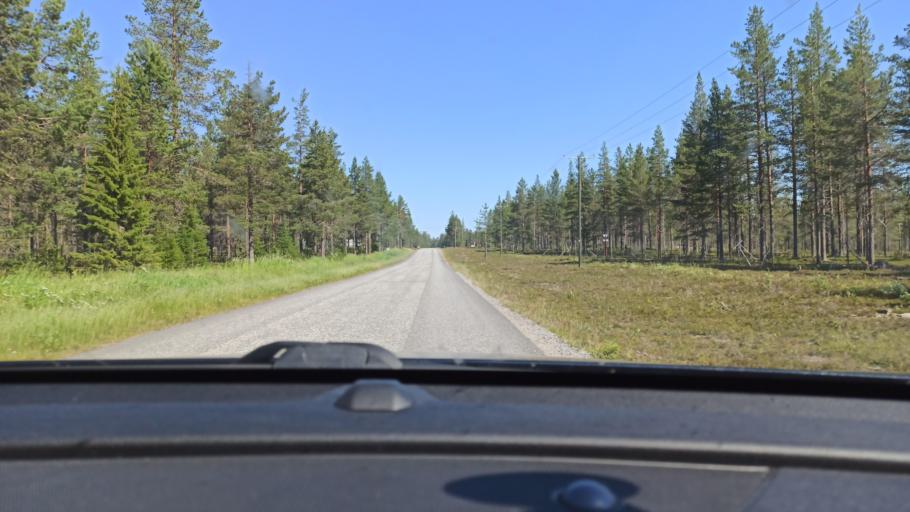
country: FI
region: Lapland
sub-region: Tunturi-Lappi
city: Kolari
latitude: 67.6526
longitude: 24.1628
